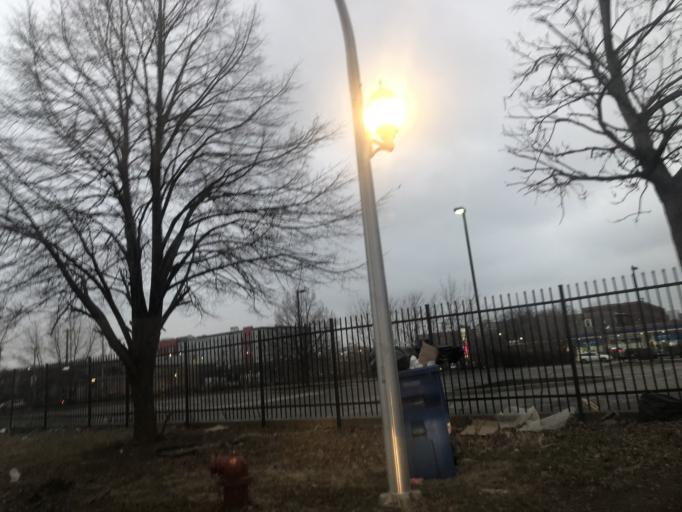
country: US
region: Illinois
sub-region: Cook County
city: Chicago
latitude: 41.7795
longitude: -87.6035
